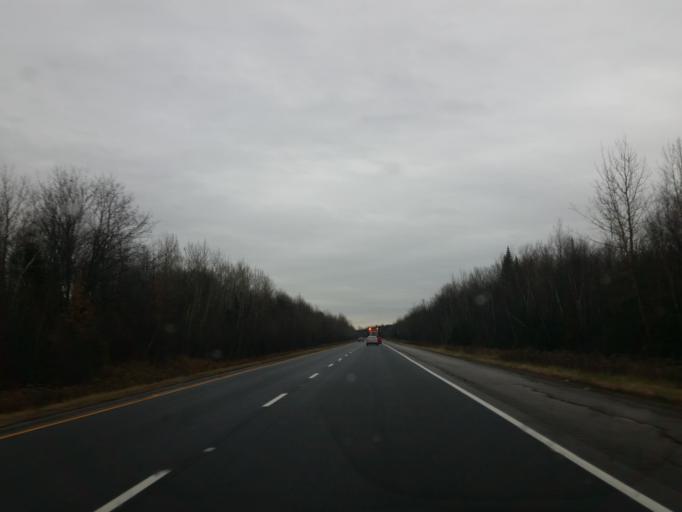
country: CA
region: Quebec
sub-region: Capitale-Nationale
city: Cap-Sante
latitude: 46.6939
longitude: -71.8215
